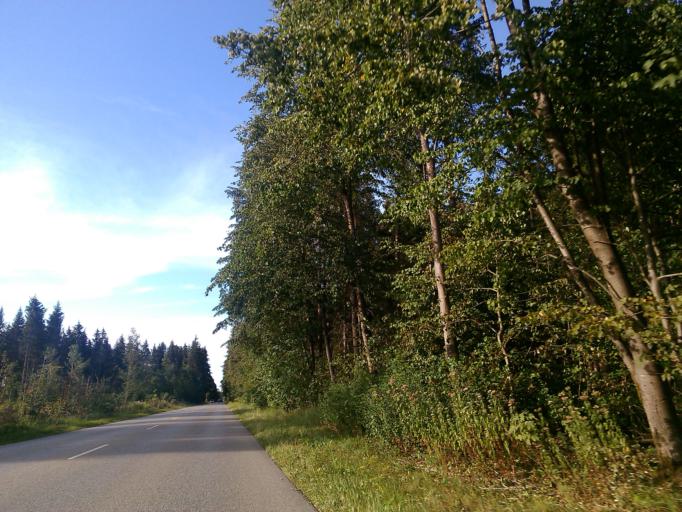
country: DE
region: Bavaria
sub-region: Upper Bavaria
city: Germering
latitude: 48.1094
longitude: 11.3743
